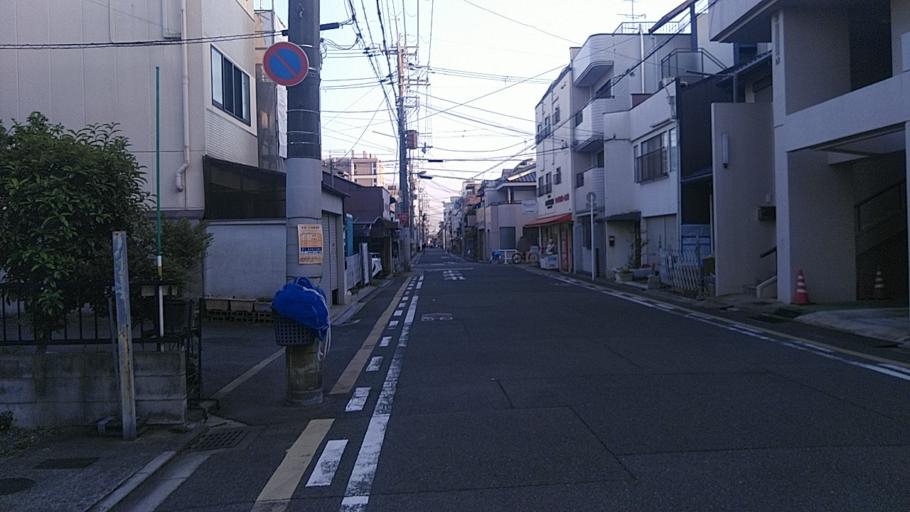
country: JP
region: Kyoto
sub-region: Kyoto-shi
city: Kamigyo-ku
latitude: 35.0323
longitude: 135.7579
